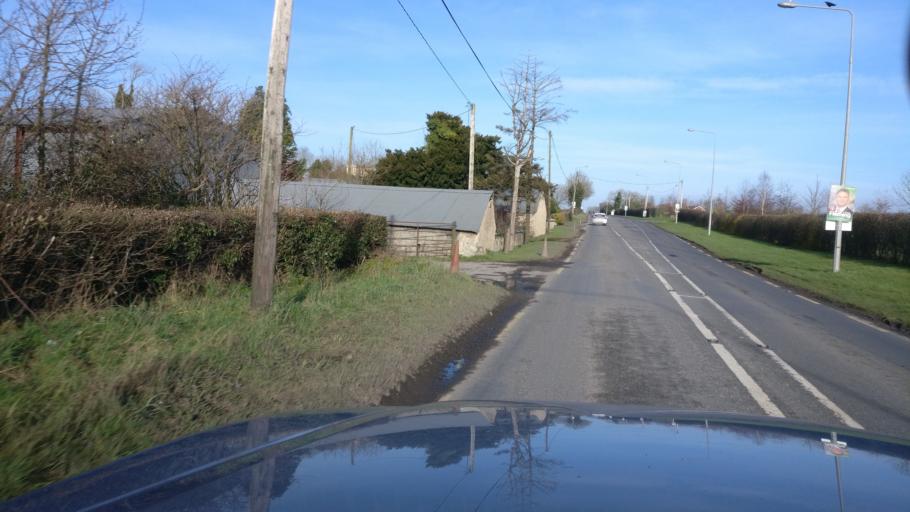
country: IE
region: Leinster
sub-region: Laois
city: Portlaoise
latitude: 53.0249
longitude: -7.2681
